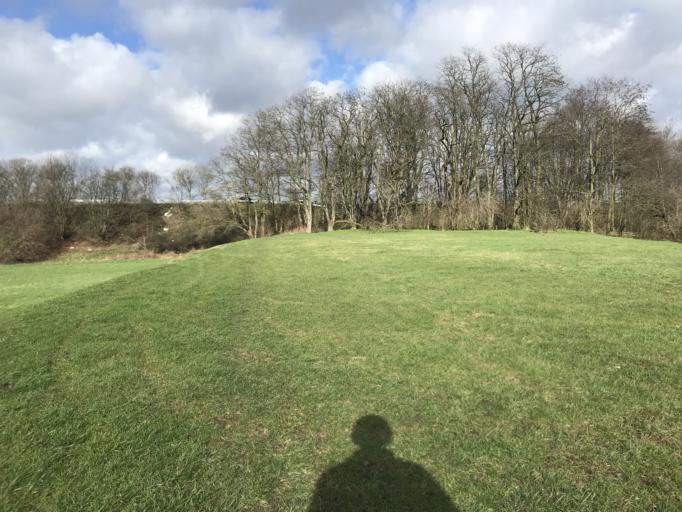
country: DE
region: North Rhine-Westphalia
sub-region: Regierungsbezirk Dusseldorf
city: Krefeld
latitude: 51.3525
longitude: 6.6661
